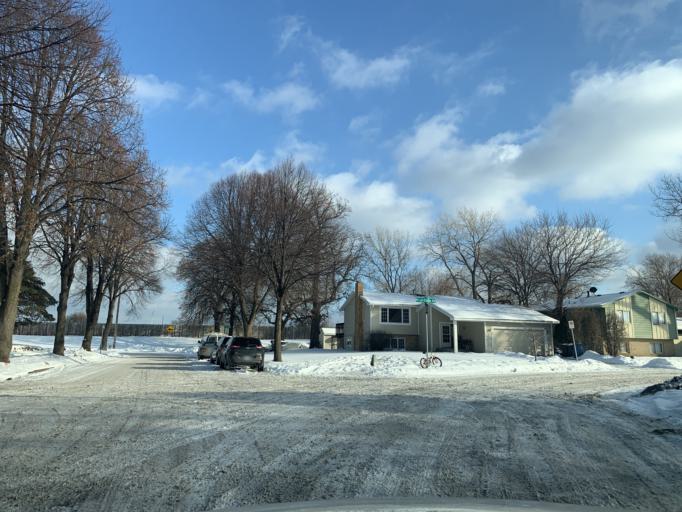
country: US
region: Minnesota
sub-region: Hennepin County
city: Minneapolis
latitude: 44.9974
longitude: -93.2852
